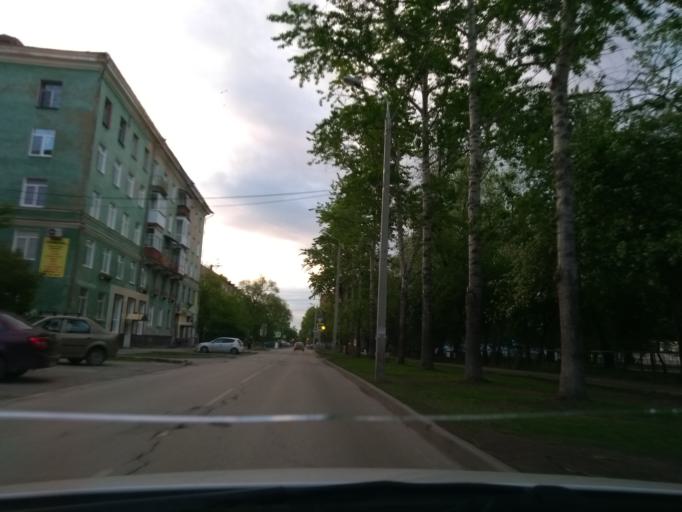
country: RU
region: Perm
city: Perm
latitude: 57.9974
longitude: 56.2574
